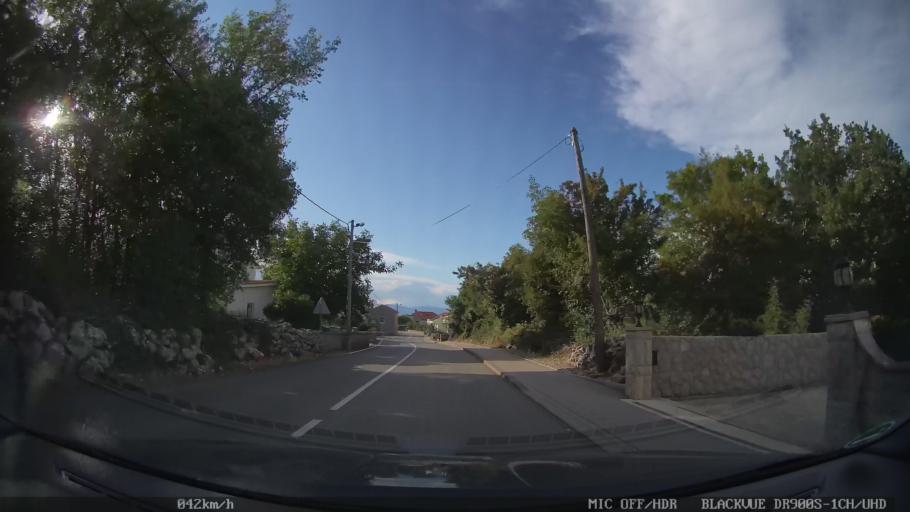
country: HR
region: Primorsko-Goranska
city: Njivice
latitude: 45.0993
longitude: 14.5296
